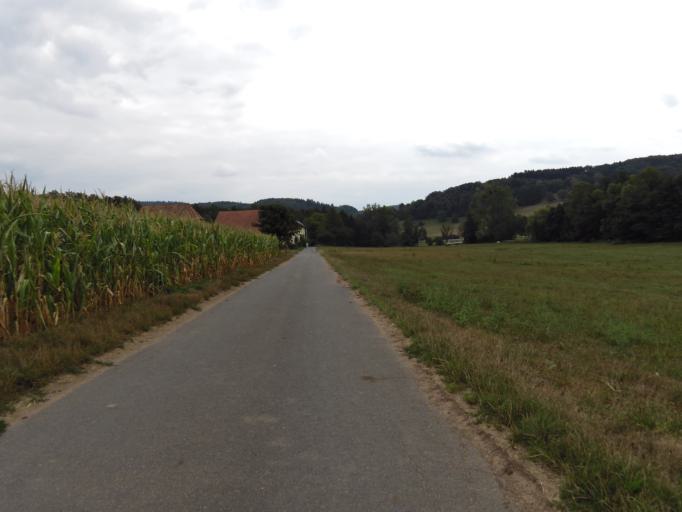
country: DE
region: Hesse
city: Reichelsheim
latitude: 49.7094
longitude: 8.8533
